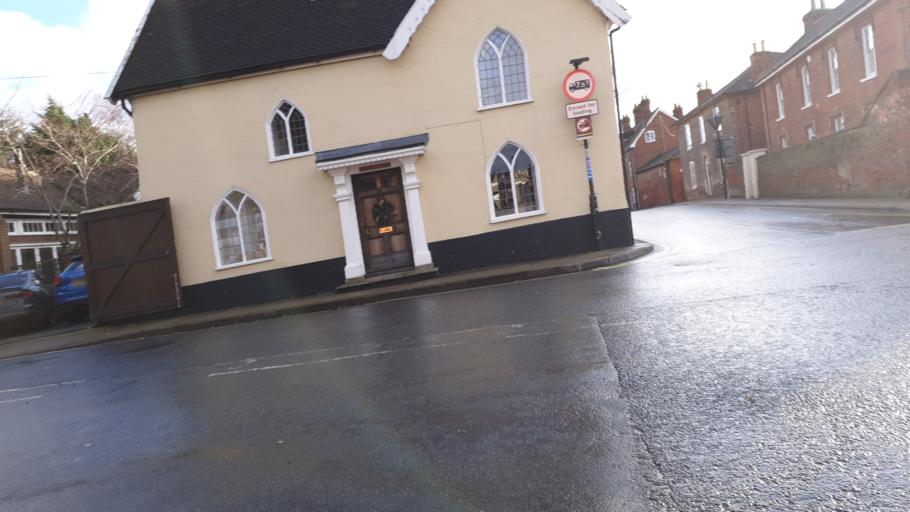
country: GB
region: England
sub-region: Suffolk
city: Hadleigh
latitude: 52.0413
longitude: 0.9558
